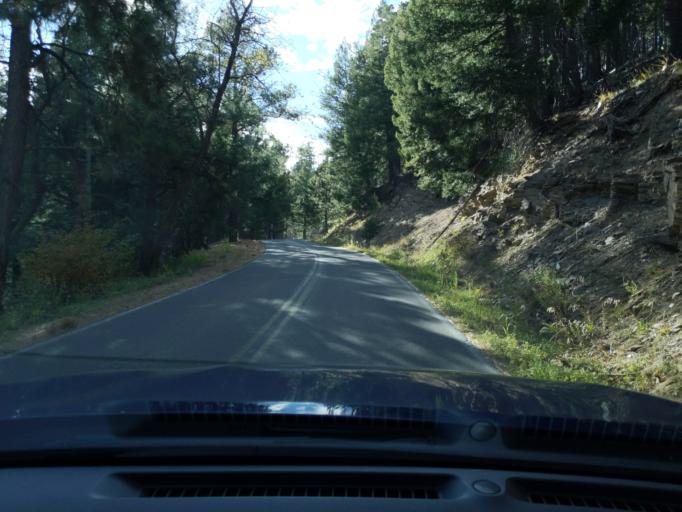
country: US
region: Arizona
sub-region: Pima County
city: Catalina
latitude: 32.4478
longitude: -110.7847
